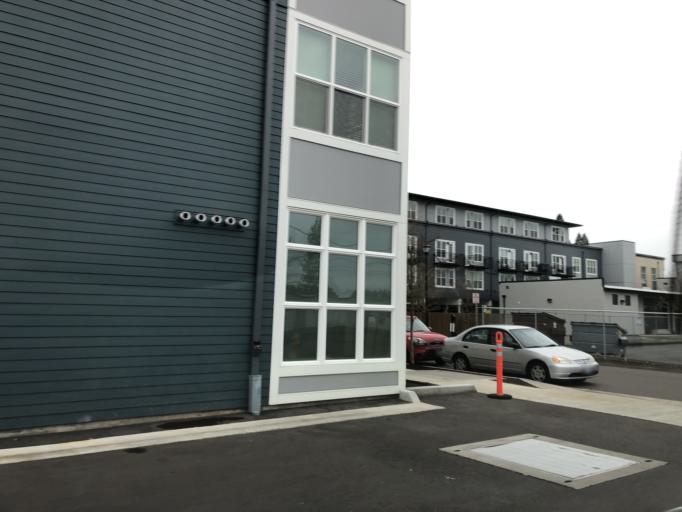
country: US
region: Oregon
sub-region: Washington County
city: Tigard
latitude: 45.4272
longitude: -122.7701
